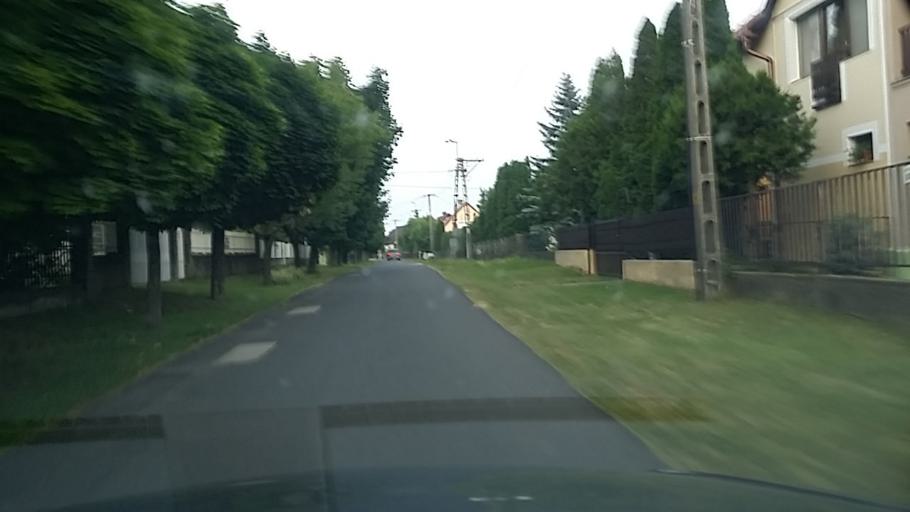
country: HU
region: Zala
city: Vonyarcvashegy
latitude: 46.7607
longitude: 17.3097
